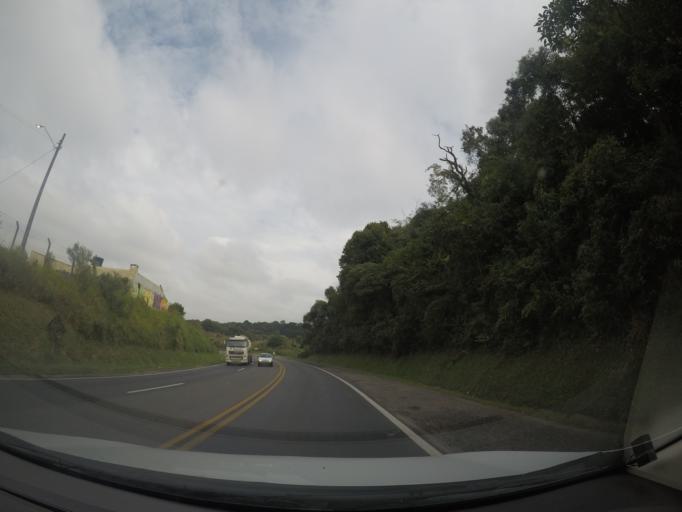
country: BR
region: Parana
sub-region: Colombo
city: Colombo
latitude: -25.3417
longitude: -49.2240
